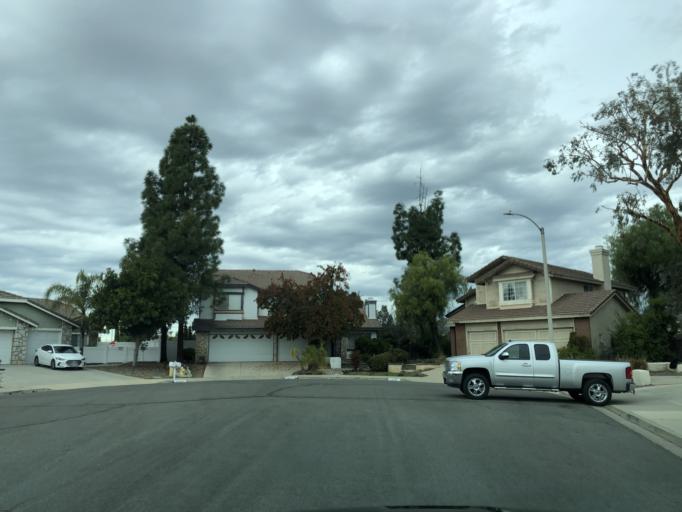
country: US
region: California
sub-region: Riverside County
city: Wildomar
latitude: 33.6098
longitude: -117.2642
